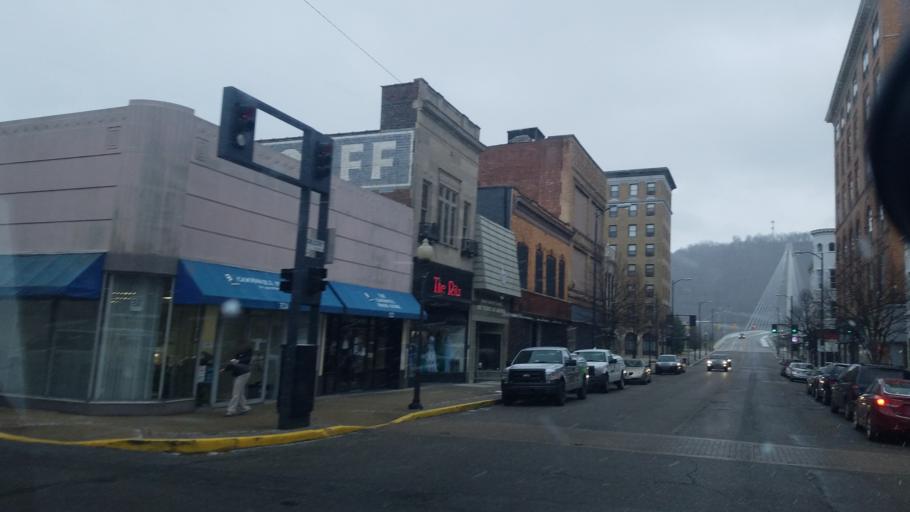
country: US
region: Ohio
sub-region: Scioto County
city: Portsmouth
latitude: 38.7332
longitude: -82.9966
